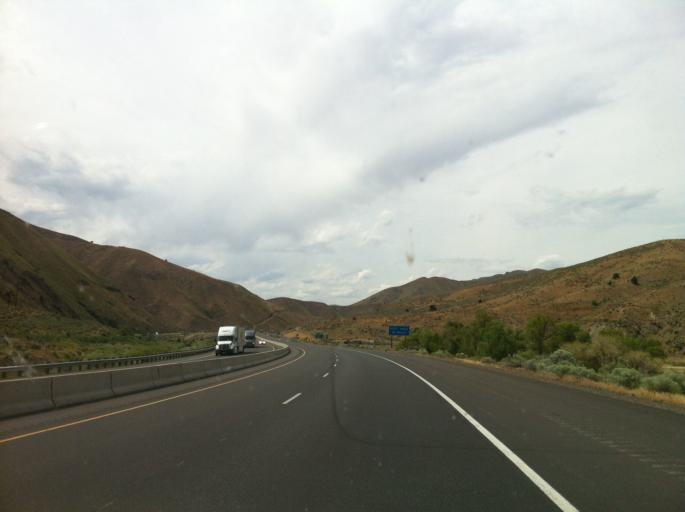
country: US
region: Idaho
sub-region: Washington County
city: Weiser
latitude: 44.4227
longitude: -117.3113
